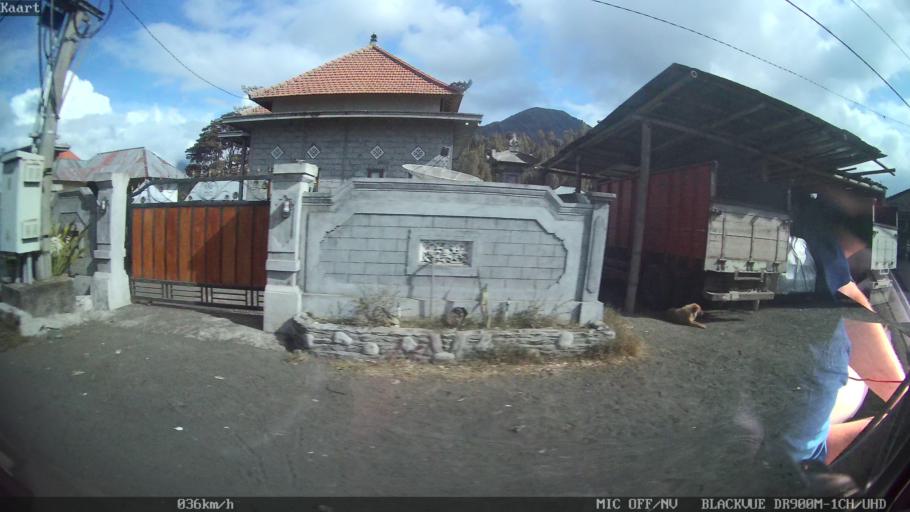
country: ID
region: Bali
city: Banjar Trunyan
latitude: -8.2163
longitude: 115.3834
